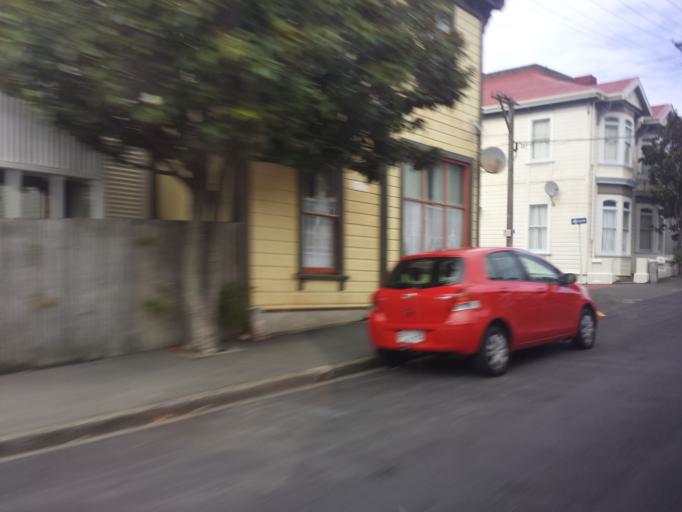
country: NZ
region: Wellington
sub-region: Wellington City
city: Wellington
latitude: -41.2970
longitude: 174.7852
